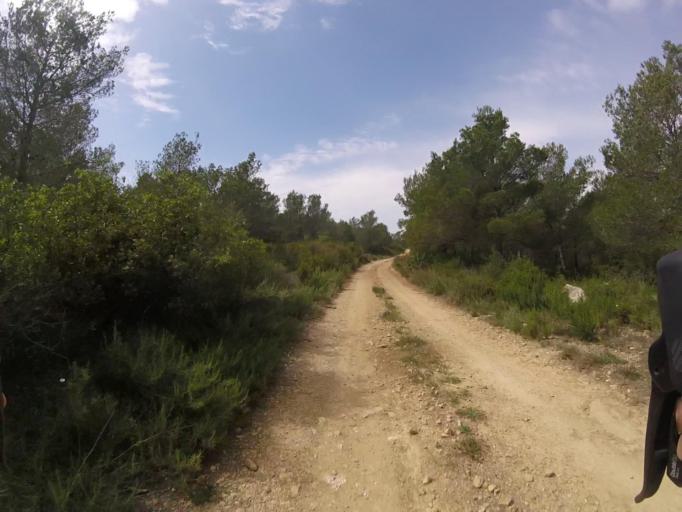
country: ES
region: Valencia
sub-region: Provincia de Castello
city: Cuevas de Vinroma
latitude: 40.2742
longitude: 0.1188
